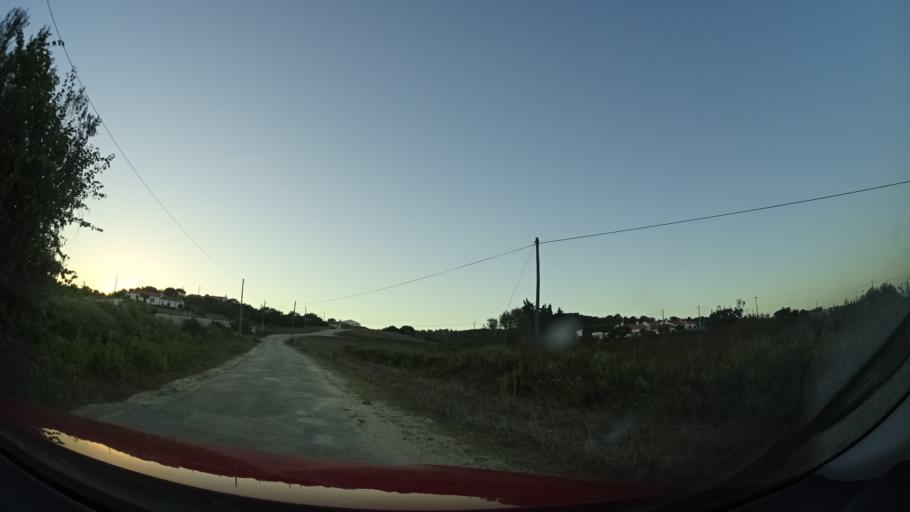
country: PT
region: Faro
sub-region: Aljezur
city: Aljezur
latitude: 37.2381
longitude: -8.8300
